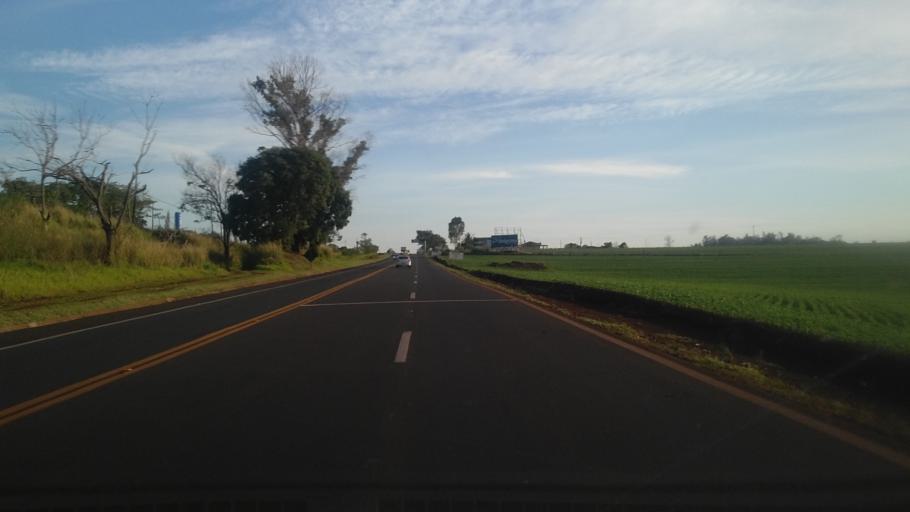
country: BR
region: Parana
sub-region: Assai
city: Assai
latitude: -23.2228
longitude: -50.6718
